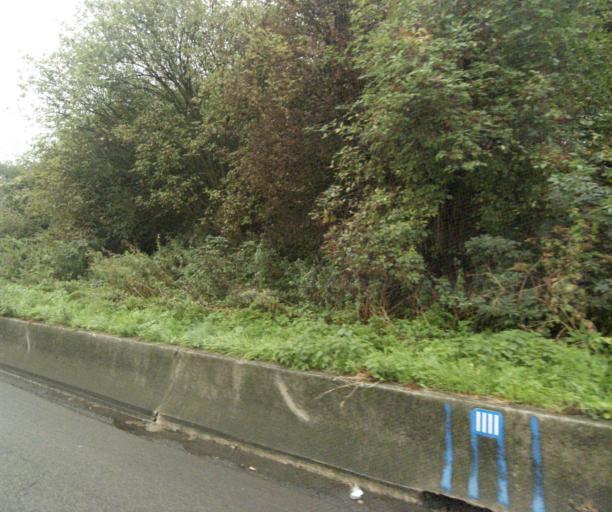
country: FR
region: Nord-Pas-de-Calais
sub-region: Departement du Nord
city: Ronchin
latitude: 50.6160
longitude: 3.0823
